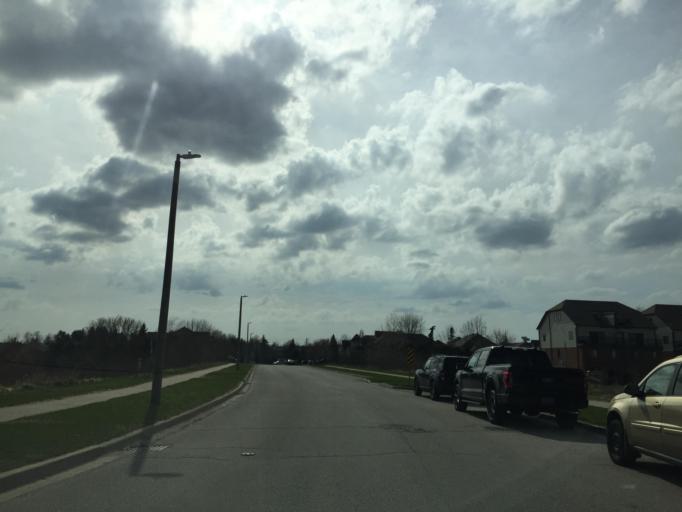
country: CA
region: Ontario
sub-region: Wellington County
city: Guelph
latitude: 43.4979
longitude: -80.2307
